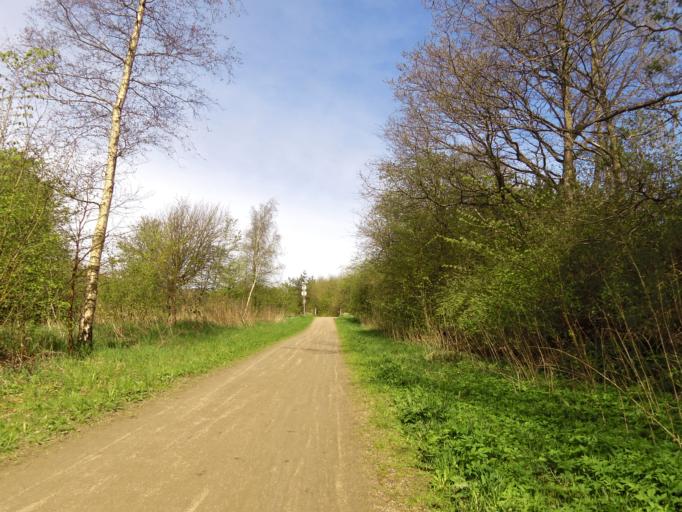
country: DK
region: Central Jutland
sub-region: Skive Kommune
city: Skive
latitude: 56.5790
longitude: 9.0256
